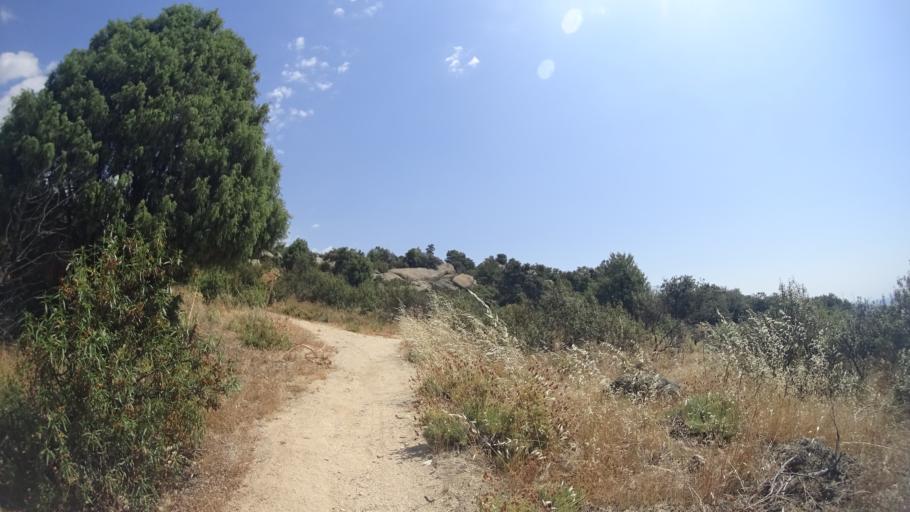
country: ES
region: Madrid
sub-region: Provincia de Madrid
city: Torrelodones
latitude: 40.5988
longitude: -3.9262
